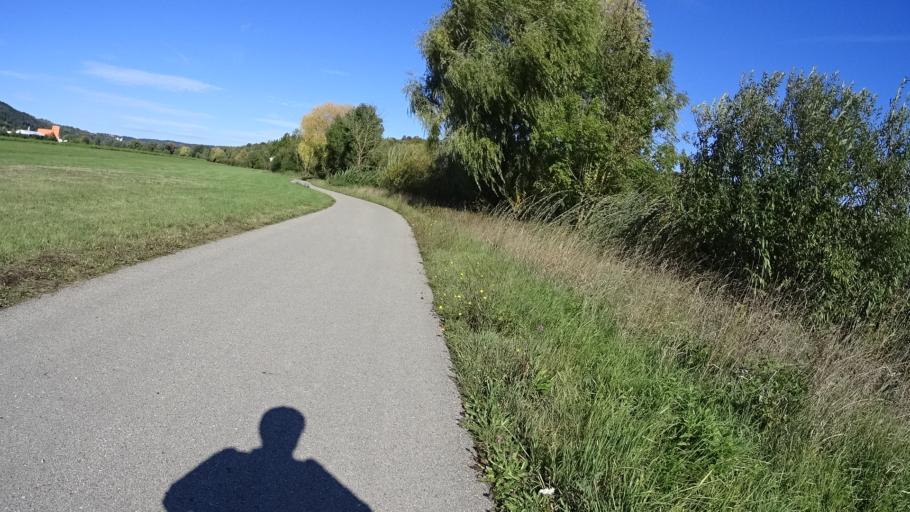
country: DE
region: Bavaria
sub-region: Upper Bavaria
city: Eichstaett
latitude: 48.8767
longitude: 11.2190
